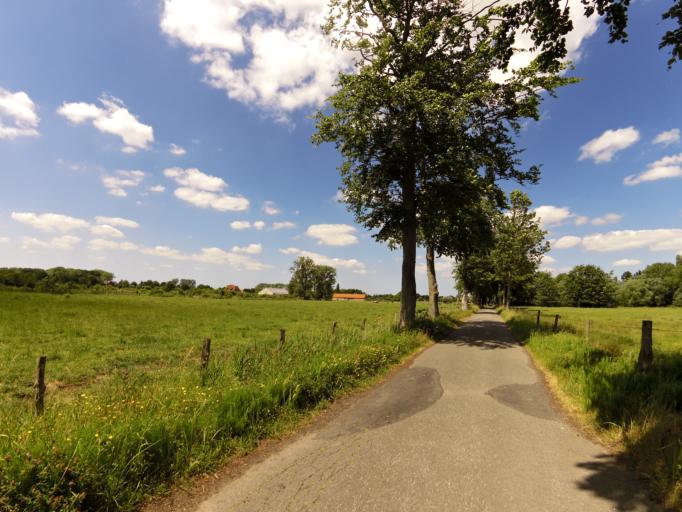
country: BE
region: Flanders
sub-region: Provincie West-Vlaanderen
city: Zedelgem
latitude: 51.1571
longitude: 3.1198
